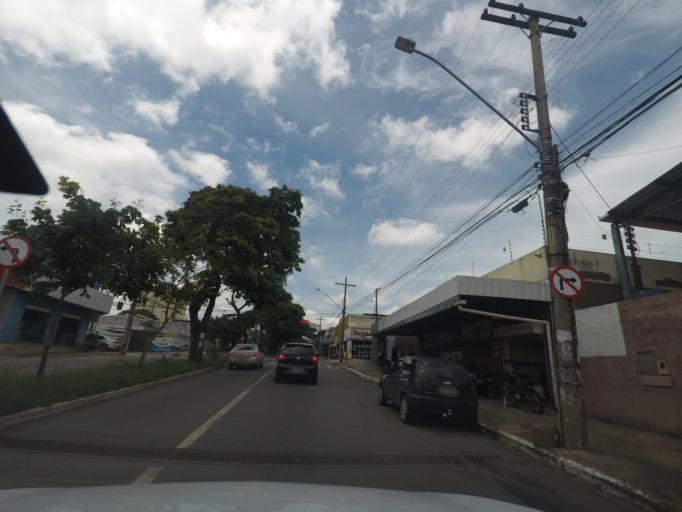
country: BR
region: Goias
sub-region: Goiania
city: Goiania
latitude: -16.6676
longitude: -49.2370
